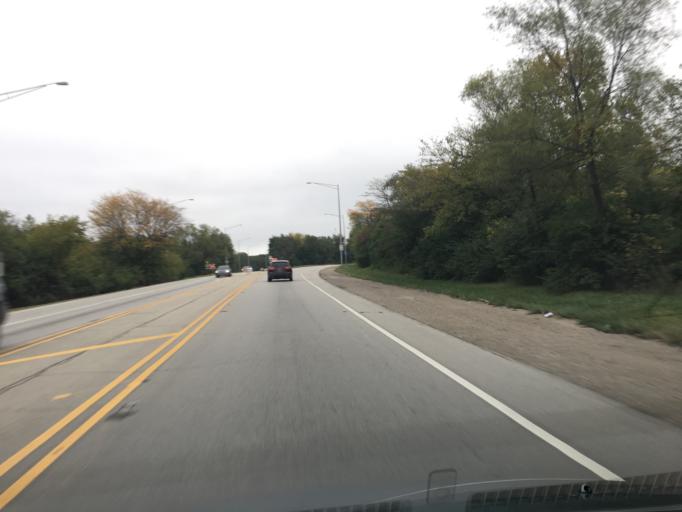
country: US
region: Illinois
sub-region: Will County
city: Plainfield
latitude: 41.6333
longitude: -88.1669
